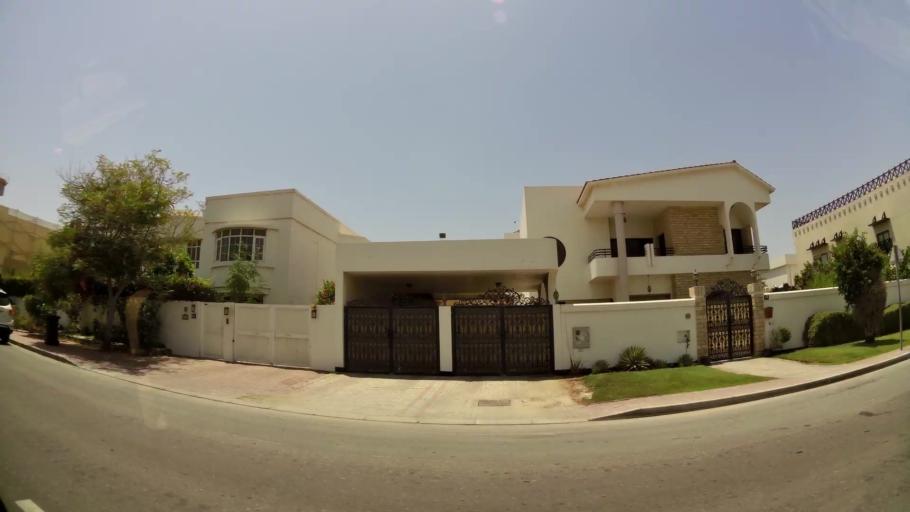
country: AE
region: Dubai
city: Dubai
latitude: 25.1874
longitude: 55.2336
